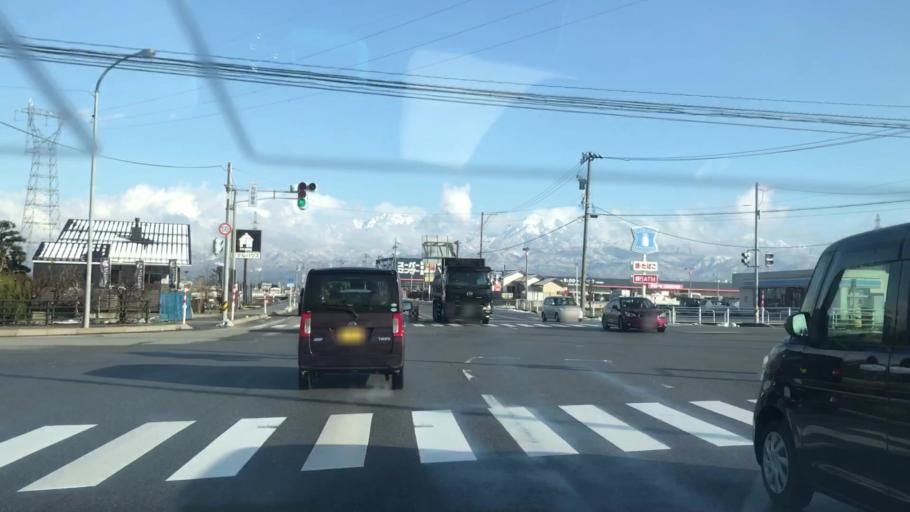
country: JP
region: Toyama
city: Kamiichi
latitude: 36.6865
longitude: 137.2917
